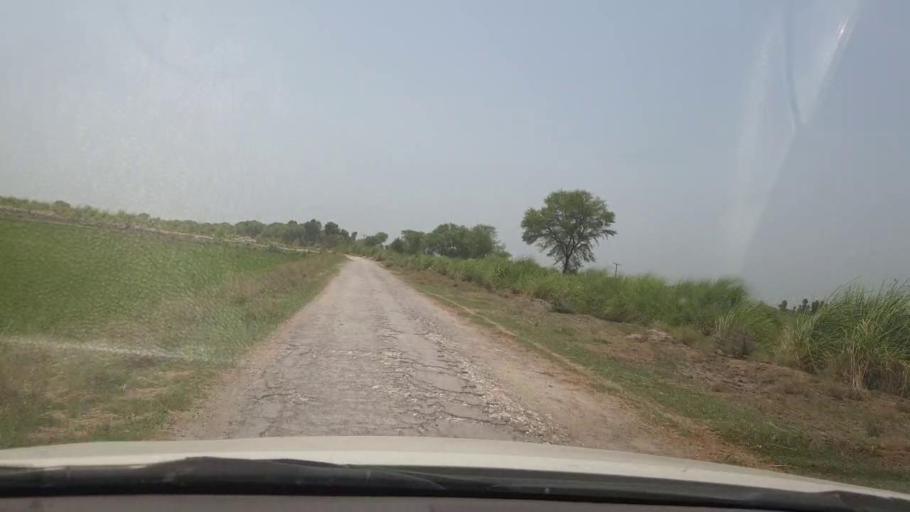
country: PK
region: Sindh
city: Shikarpur
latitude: 28.0851
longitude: 68.5578
